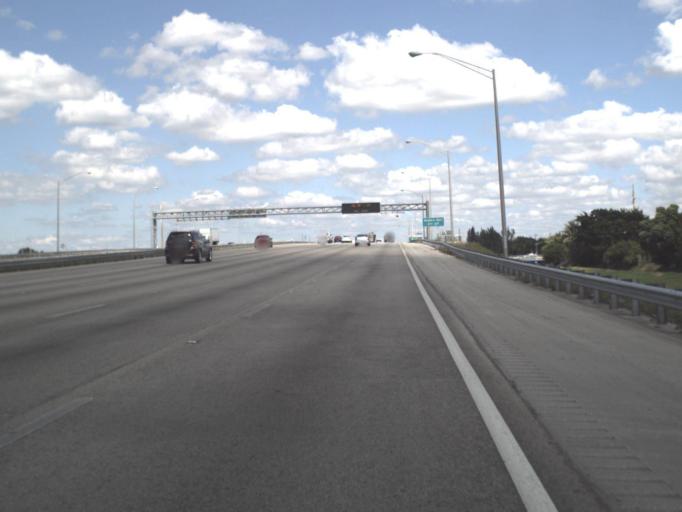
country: US
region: Florida
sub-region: Miami-Dade County
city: Sweetwater
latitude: 25.7652
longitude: -80.3853
